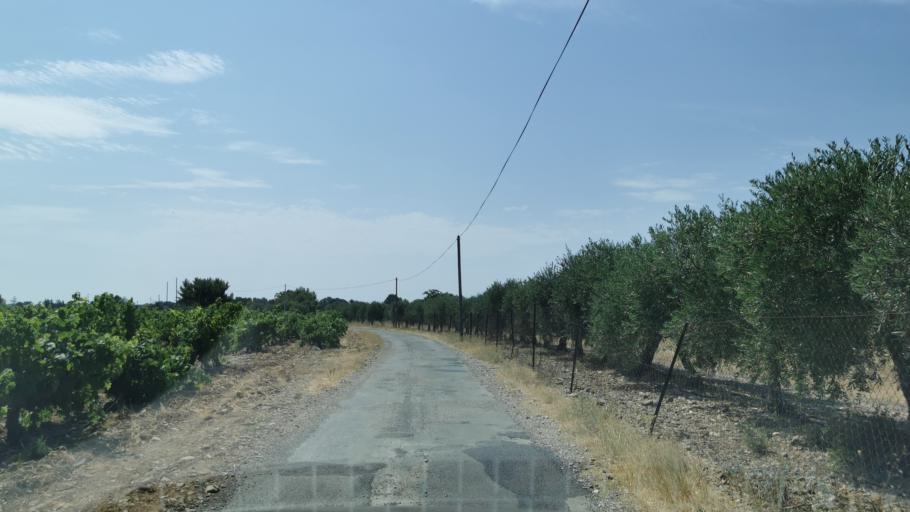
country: FR
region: Languedoc-Roussillon
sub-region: Departement de l'Aude
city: Bize-Minervois
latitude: 43.2992
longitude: 2.8755
